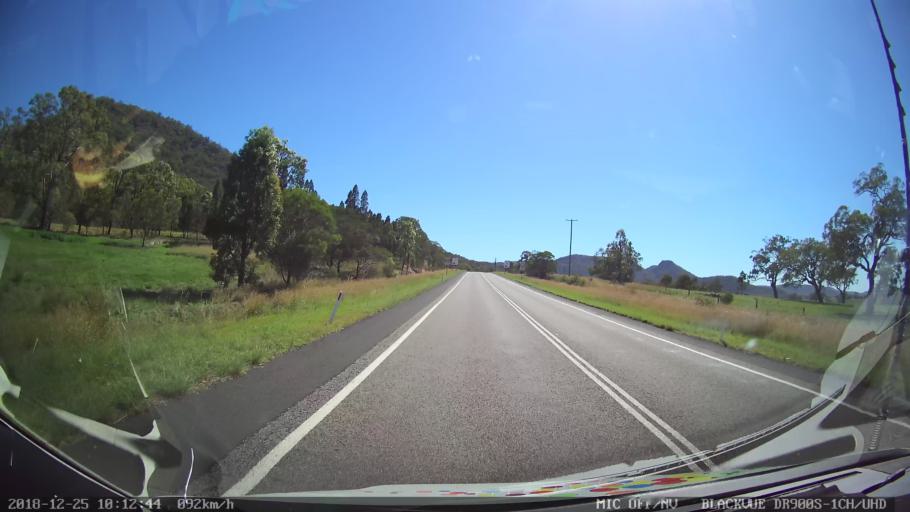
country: AU
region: New South Wales
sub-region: Muswellbrook
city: Denman
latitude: -32.3284
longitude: 150.5352
